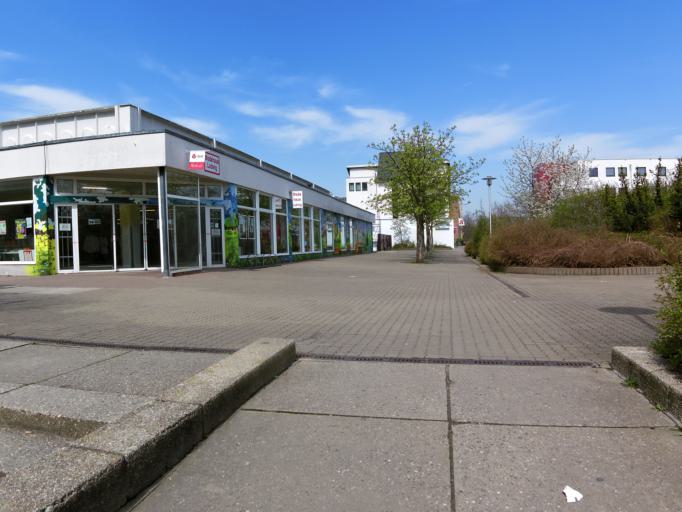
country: DE
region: Saxony
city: Markranstadt
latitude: 51.3125
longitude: 12.2654
